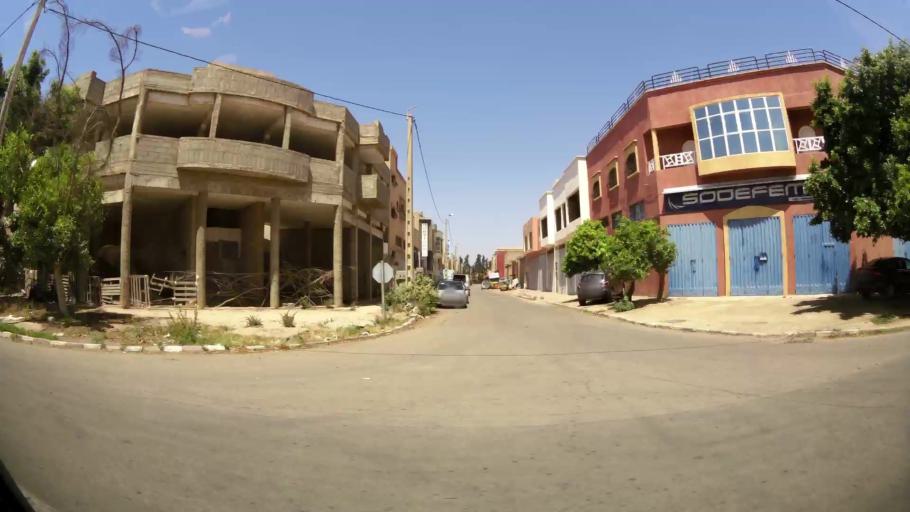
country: MA
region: Souss-Massa-Draa
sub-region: Inezgane-Ait Mellou
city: Inezgane
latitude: 30.3311
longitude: -9.4936
